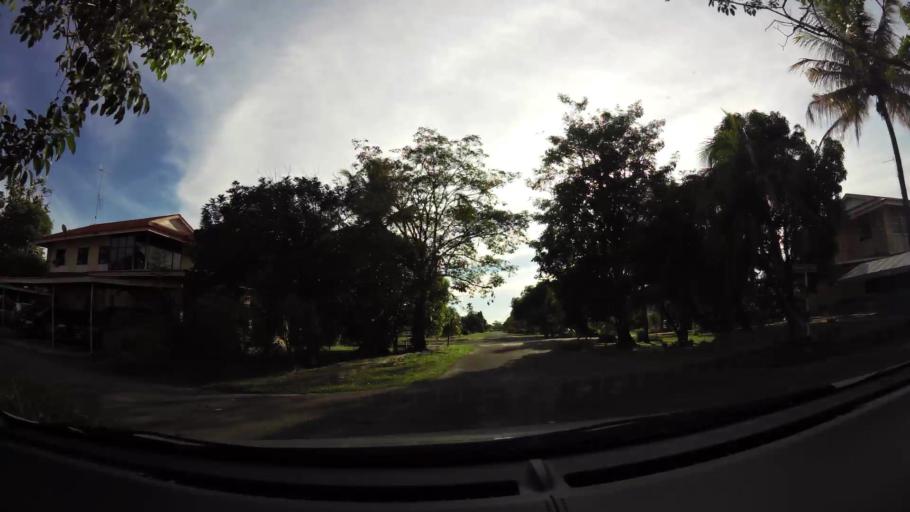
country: BN
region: Belait
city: Kuala Belait
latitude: 4.5767
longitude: 114.2241
